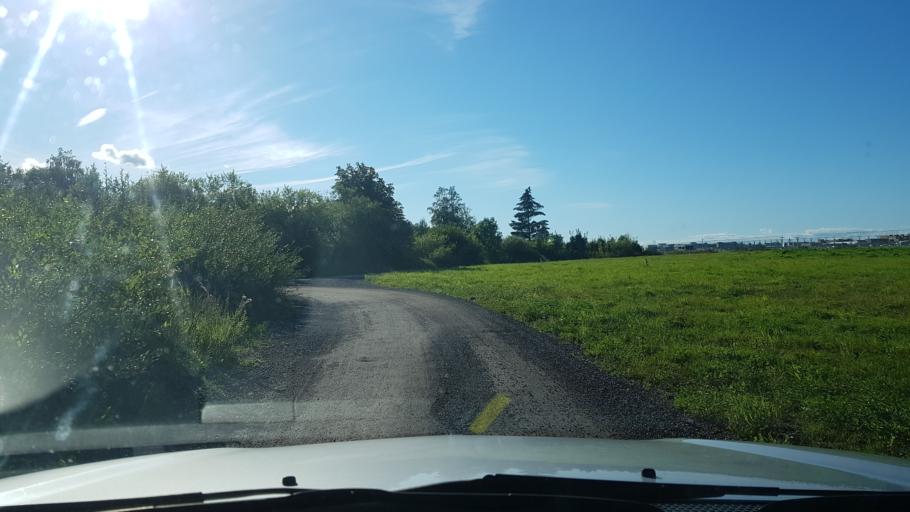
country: EE
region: Harju
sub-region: Tallinna linn
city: Kose
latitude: 59.4092
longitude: 24.8747
